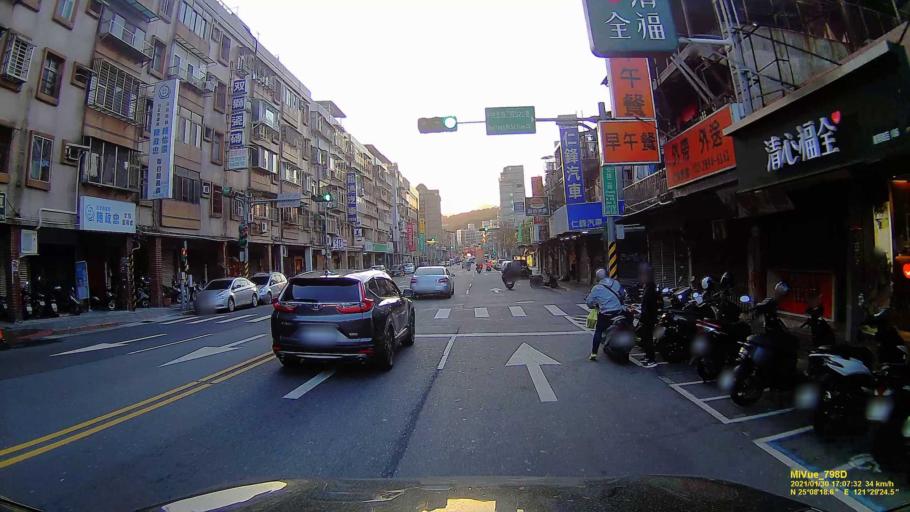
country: TW
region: Taipei
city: Taipei
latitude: 25.1385
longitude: 121.4899
